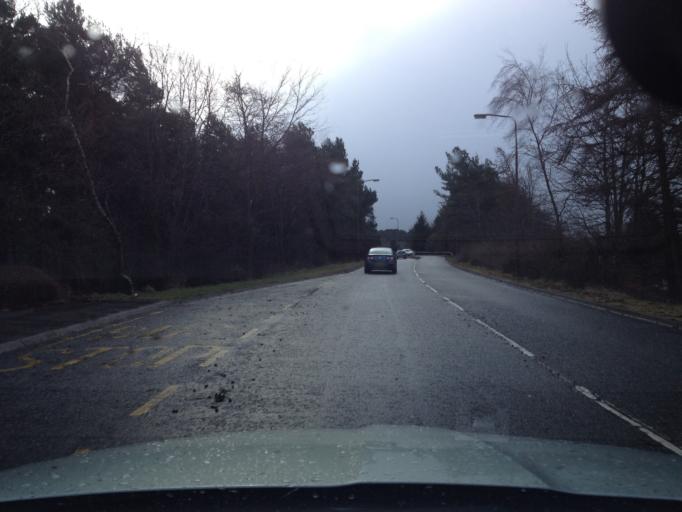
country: GB
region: Scotland
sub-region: West Lothian
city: Livingston
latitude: 55.9041
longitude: -3.5314
